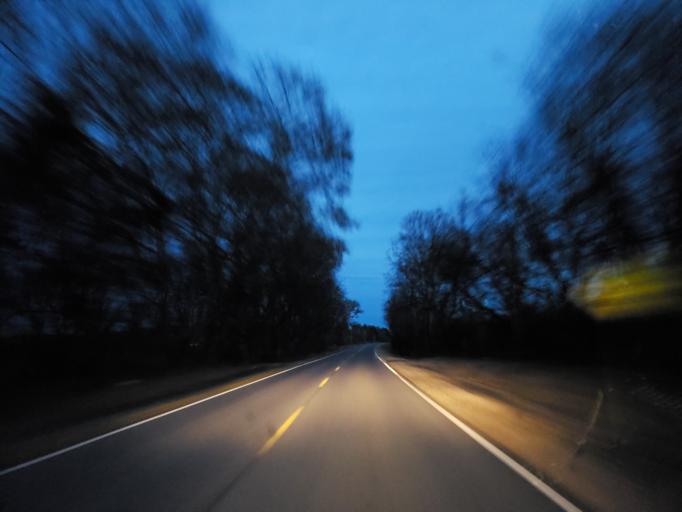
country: US
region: Alabama
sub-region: Greene County
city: Eutaw
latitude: 32.8876
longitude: -87.9438
